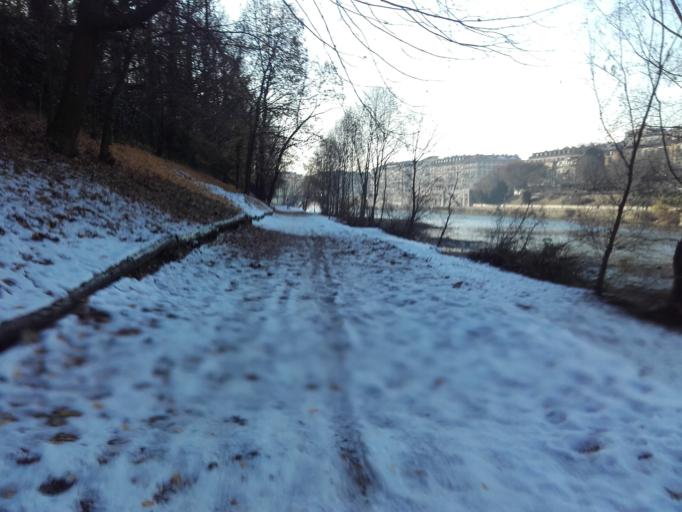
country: IT
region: Piedmont
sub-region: Provincia di Torino
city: Turin
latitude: 45.0673
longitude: 7.7023
